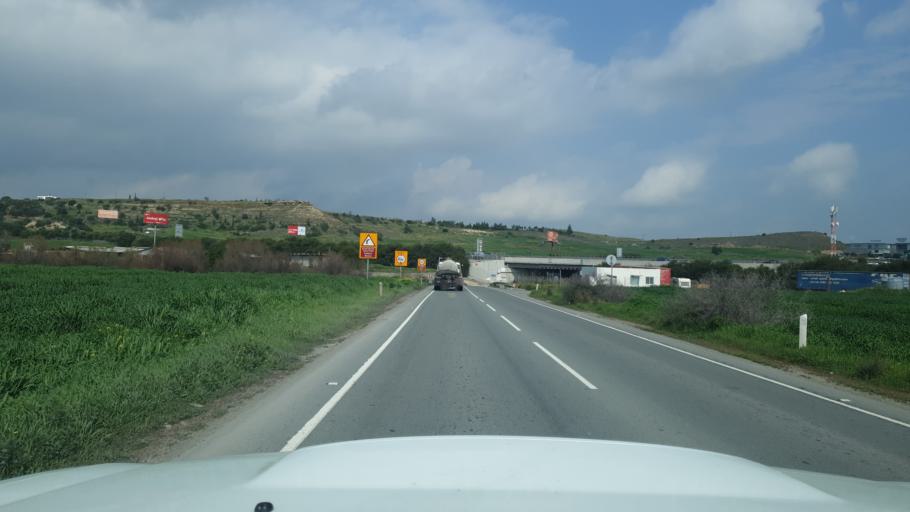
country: CY
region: Lefkosia
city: Dali
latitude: 35.0558
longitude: 33.3834
